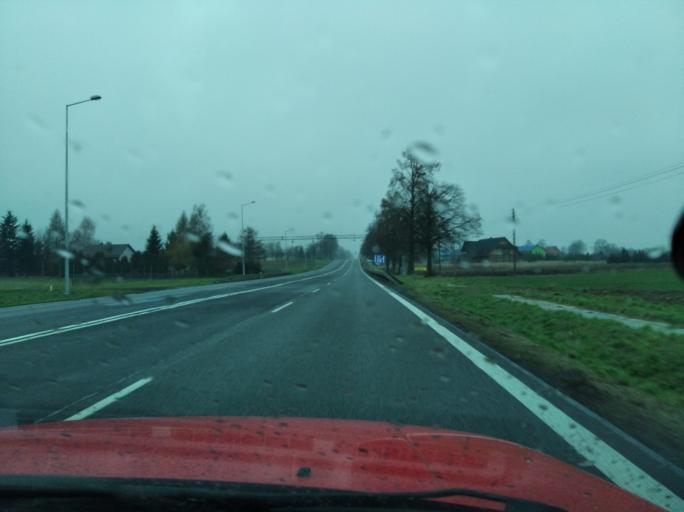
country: PL
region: Subcarpathian Voivodeship
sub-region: Powiat przeworski
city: Grzeska
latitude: 50.0631
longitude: 22.4480
